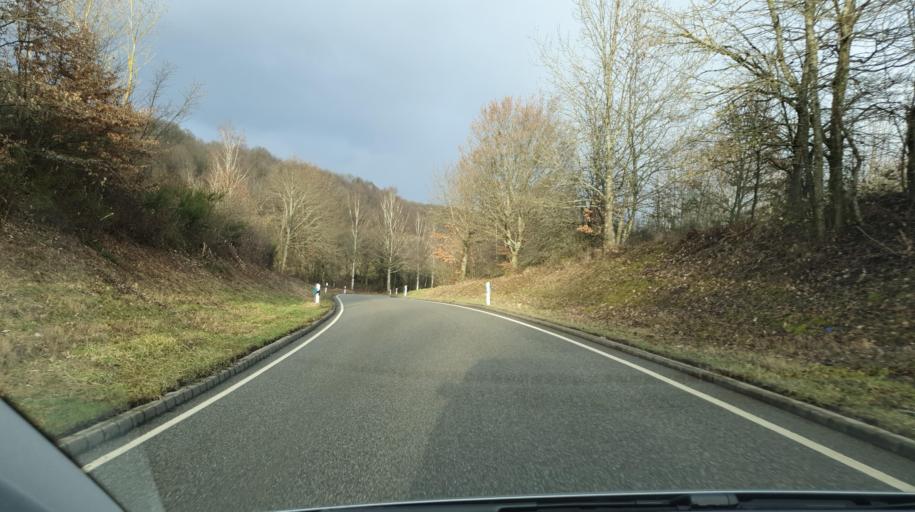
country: DE
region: Rheinland-Pfalz
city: Ulmet
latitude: 49.5795
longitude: 7.4324
